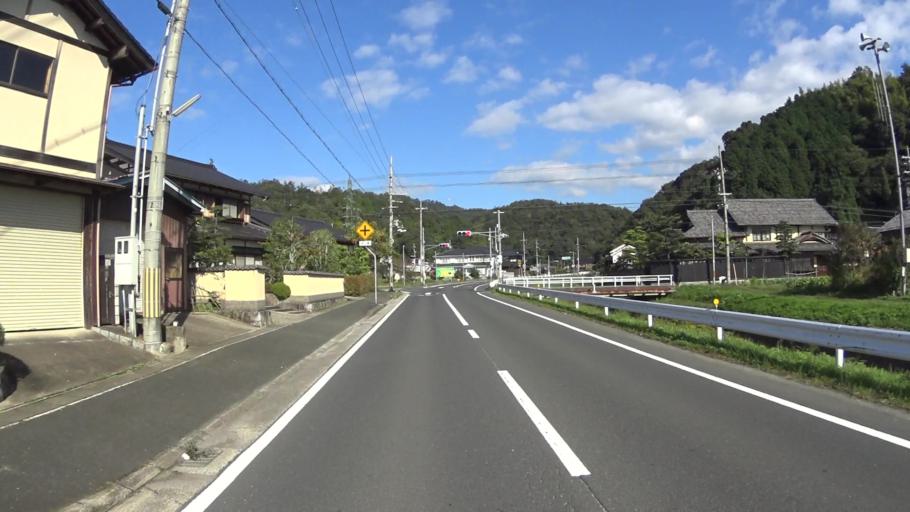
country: JP
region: Kyoto
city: Miyazu
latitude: 35.5735
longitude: 135.1609
